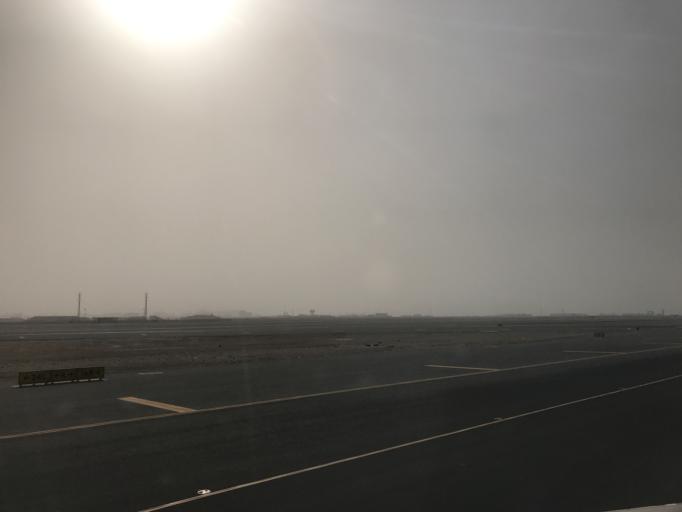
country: QA
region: Baladiyat ad Dawhah
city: Doha
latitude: 25.2795
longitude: 51.5970
